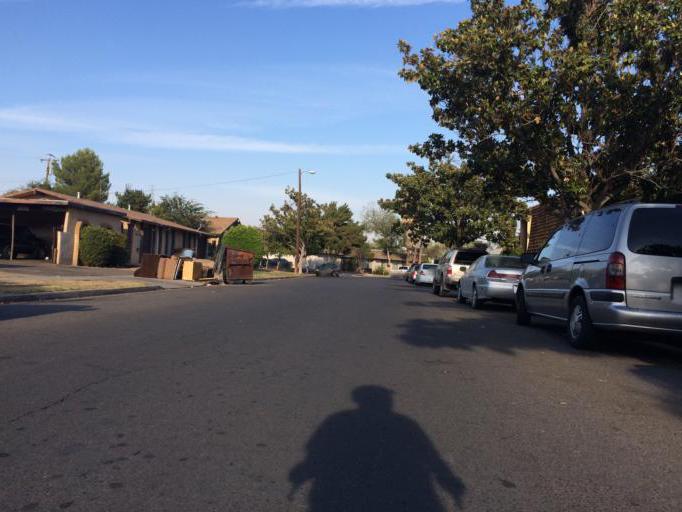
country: US
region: California
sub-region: Fresno County
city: Sunnyside
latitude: 36.7672
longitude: -119.7357
